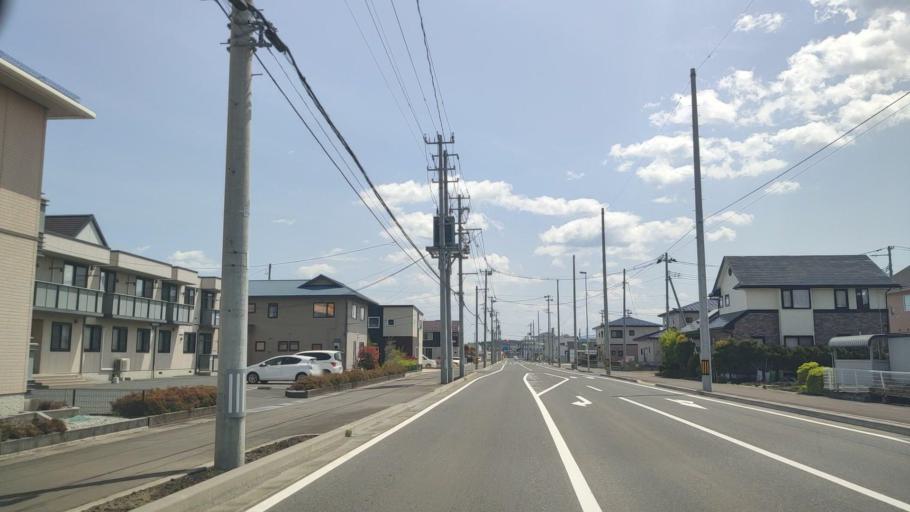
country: JP
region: Aomori
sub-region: Hachinohe Shi
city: Uchimaru
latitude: 40.5155
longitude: 141.4299
